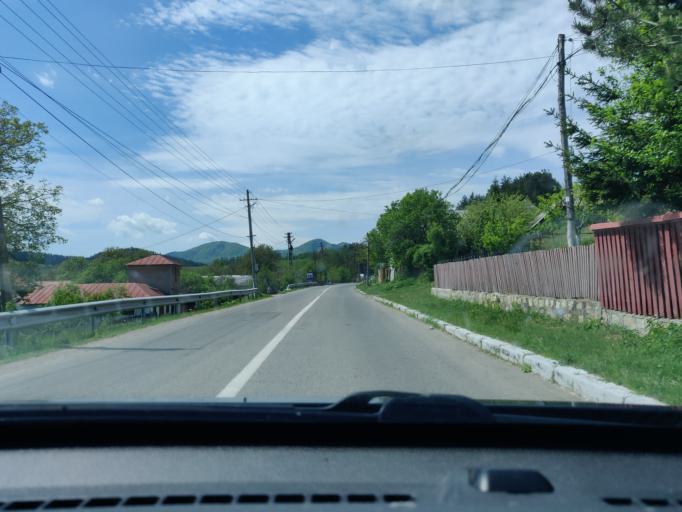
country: RO
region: Vrancea
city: Dragosloveni
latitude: 46.0021
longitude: 26.6689
